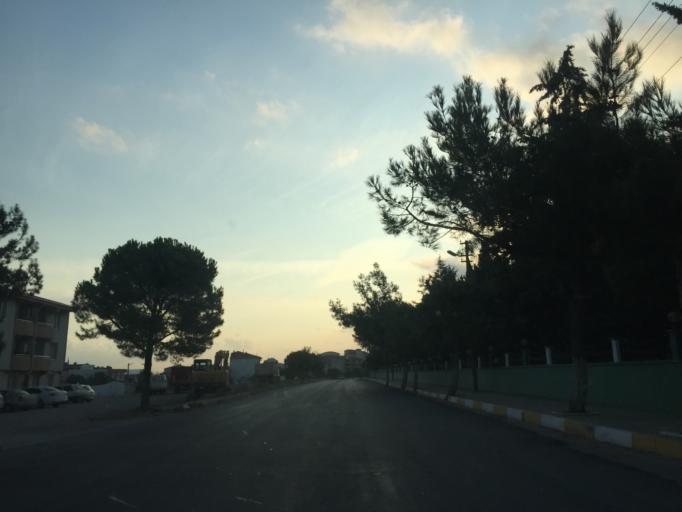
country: TR
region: Balikesir
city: Gonen
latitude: 40.0942
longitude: 27.6562
